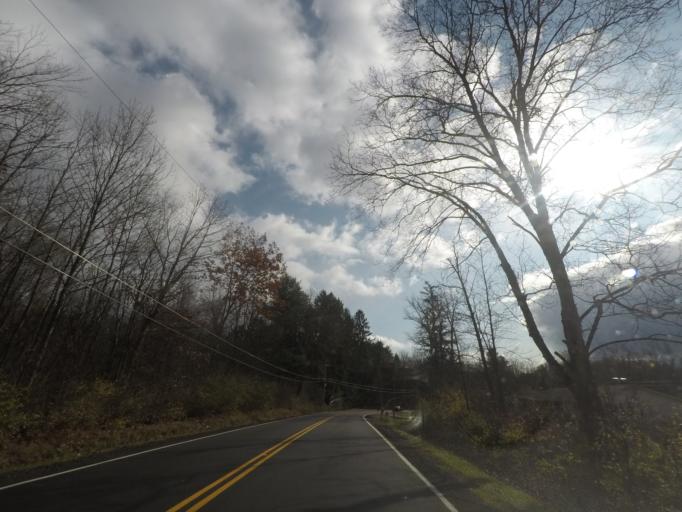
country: US
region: New York
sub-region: Saratoga County
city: Country Knolls
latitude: 42.9415
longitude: -73.8518
